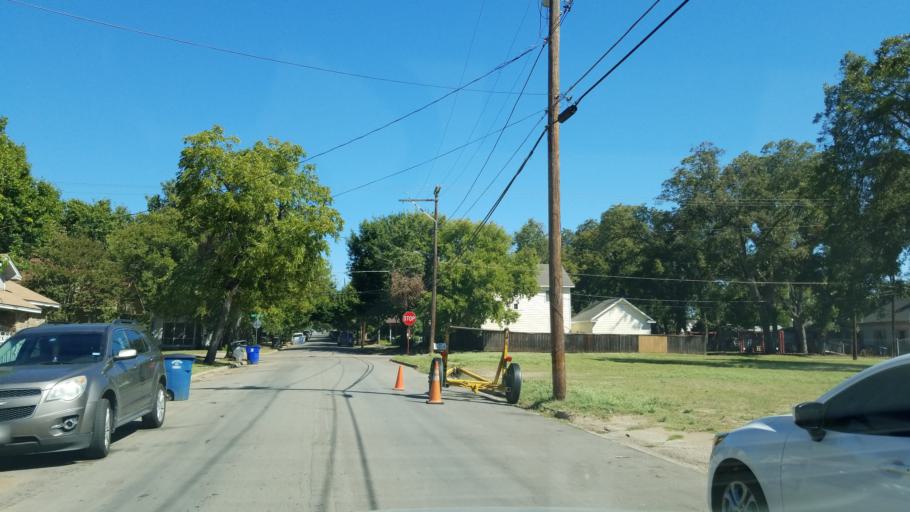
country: US
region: Texas
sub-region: Dallas County
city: Dallas
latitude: 32.7930
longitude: -96.7517
